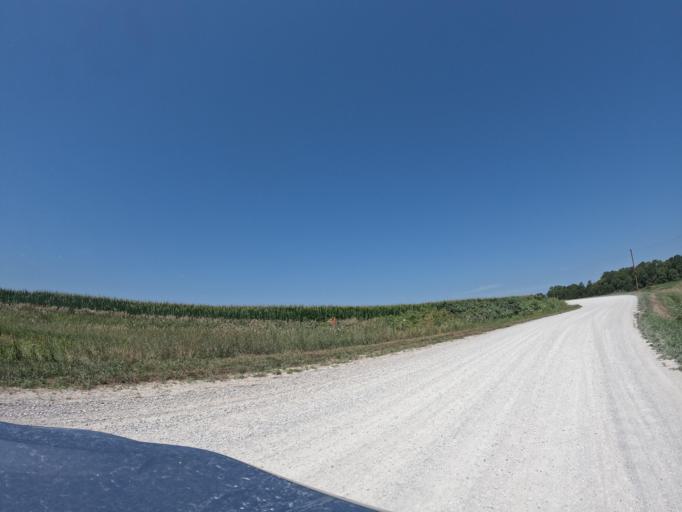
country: US
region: Iowa
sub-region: Henry County
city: Mount Pleasant
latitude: 40.8868
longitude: -91.5696
